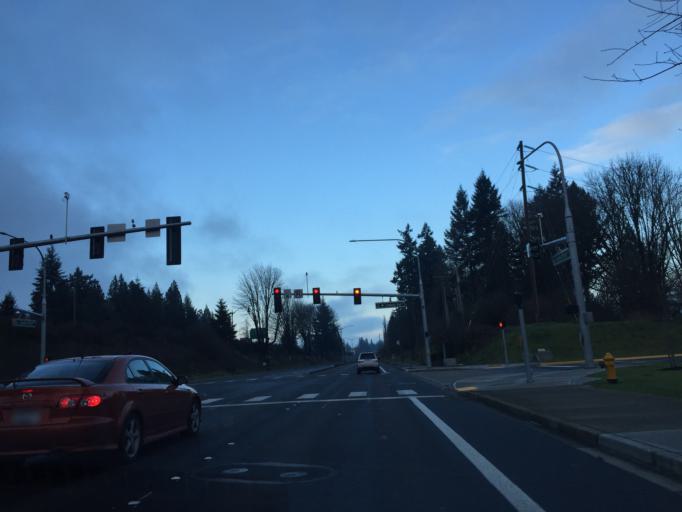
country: US
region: Washington
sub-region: Thurston County
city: Tumwater
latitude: 47.0065
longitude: -122.9077
